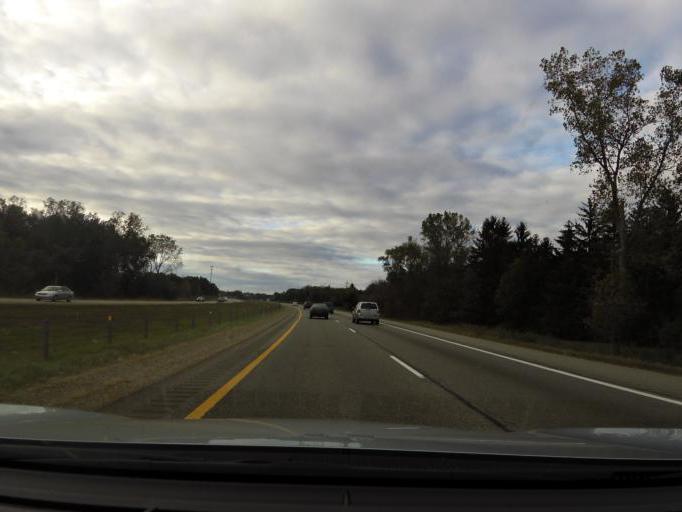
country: US
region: Michigan
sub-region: Livingston County
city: Brighton
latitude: 42.6101
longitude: -83.7419
